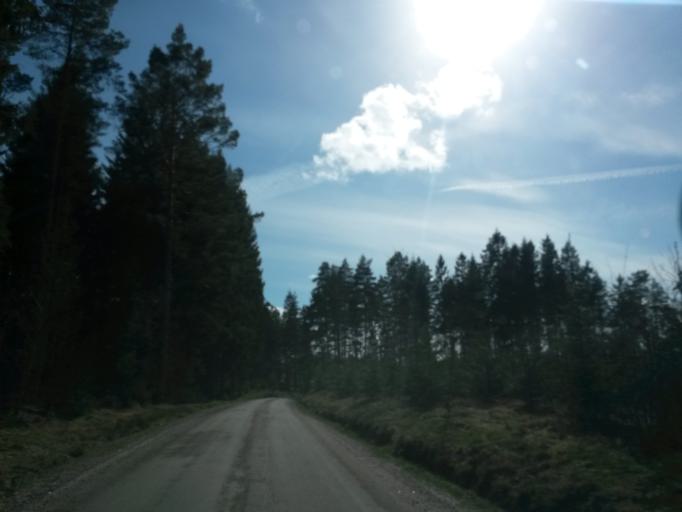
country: SE
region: Vaestra Goetaland
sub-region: Vargarda Kommun
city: Jonstorp
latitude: 57.9806
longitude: 12.7522
